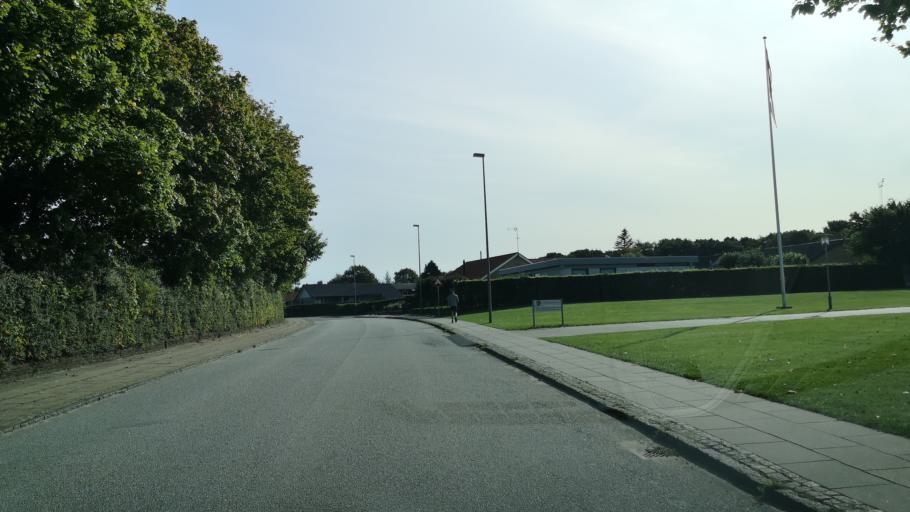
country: DK
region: Central Jutland
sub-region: Ikast-Brande Kommune
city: Ikast
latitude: 56.1479
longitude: 9.1447
